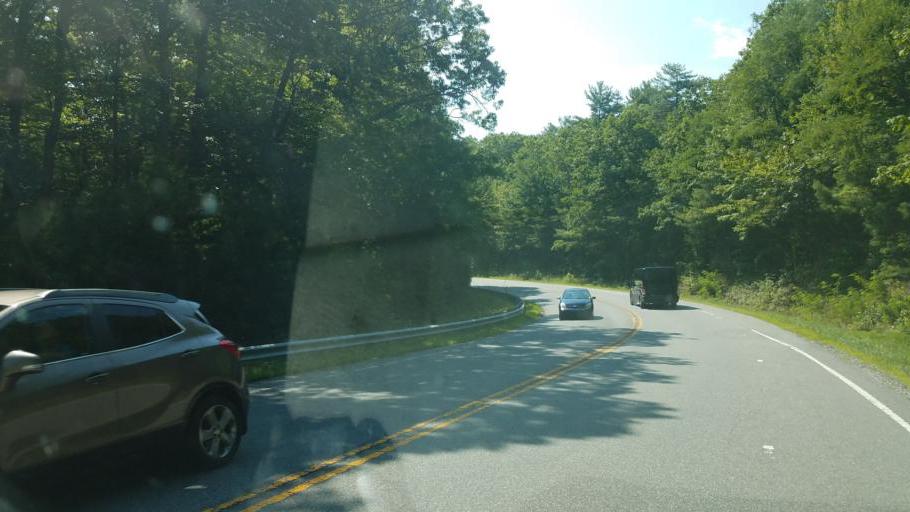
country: US
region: North Carolina
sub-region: Avery County
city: Newland
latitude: 35.9331
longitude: -81.8265
